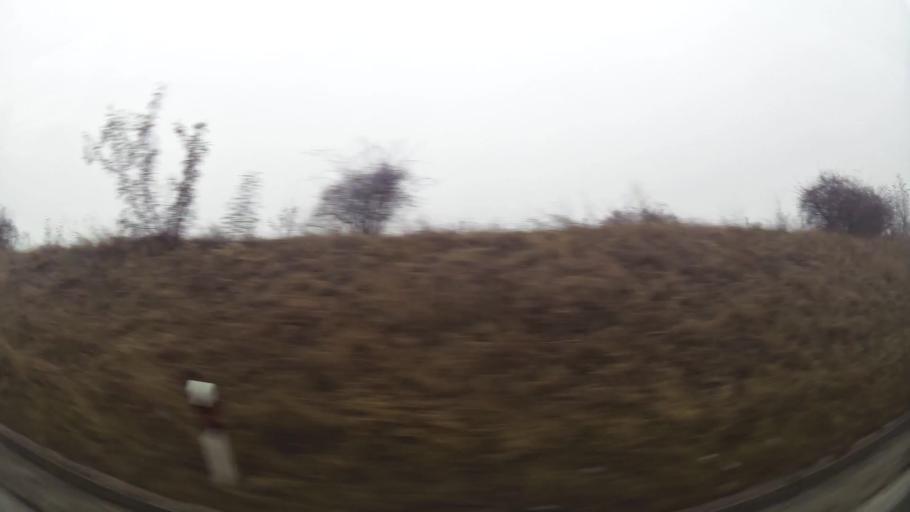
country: MK
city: Miladinovci
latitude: 41.9750
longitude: 21.6498
